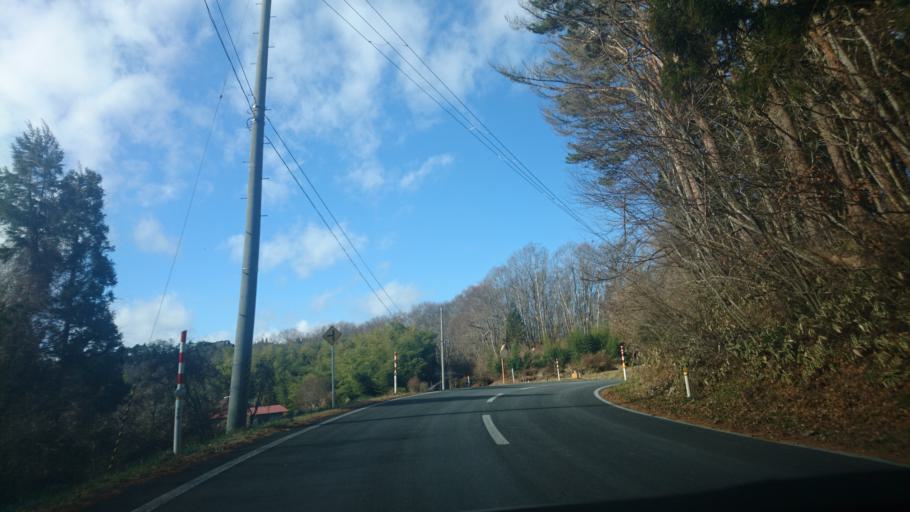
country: JP
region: Iwate
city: Ichinoseki
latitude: 38.9697
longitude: 141.3979
